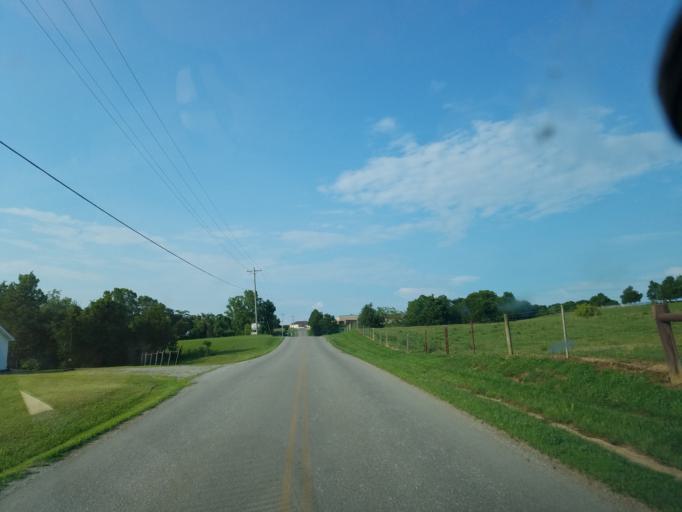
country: US
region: Ohio
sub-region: Adams County
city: West Union
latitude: 38.8939
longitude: -83.5220
